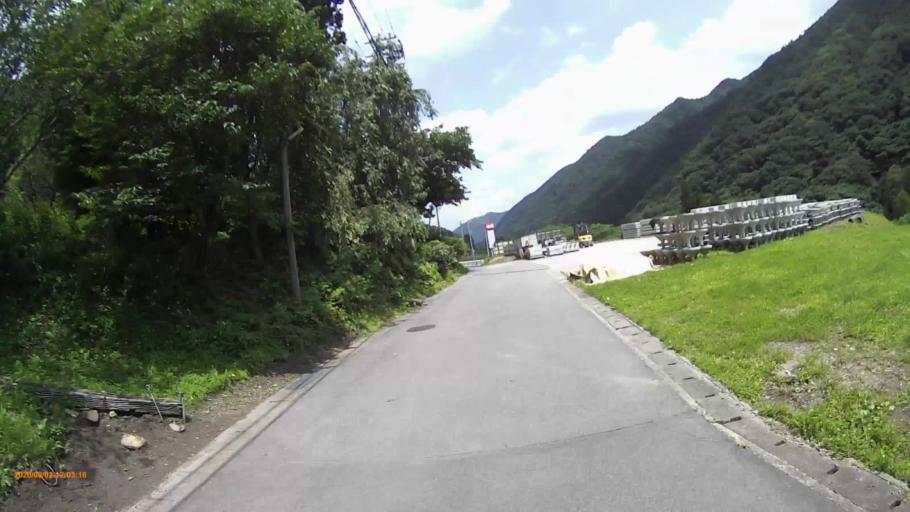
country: JP
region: Nagano
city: Shiojiri
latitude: 36.0254
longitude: 137.8701
